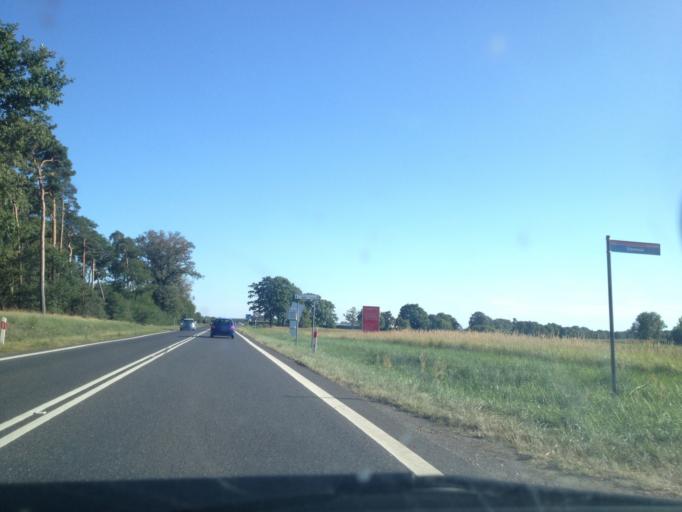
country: PL
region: Greater Poland Voivodeship
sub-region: Powiat sremski
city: Srem
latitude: 52.1346
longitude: 17.0412
